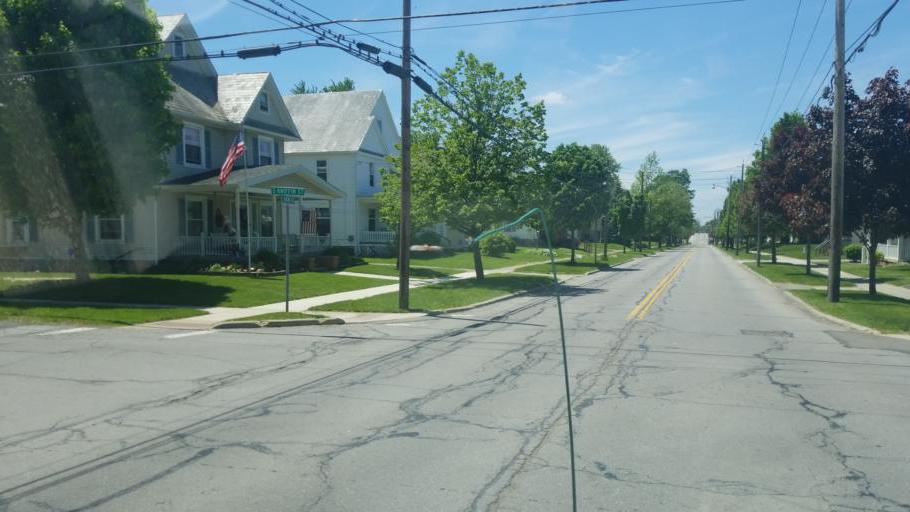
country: US
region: Ohio
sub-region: Huron County
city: Greenwich
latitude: 41.0298
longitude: -82.5107
